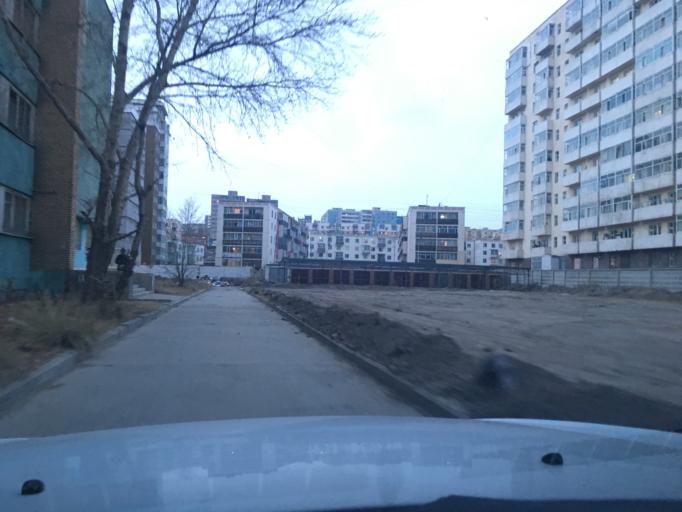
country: MN
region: Ulaanbaatar
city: Ulaanbaatar
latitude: 47.9153
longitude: 106.8611
